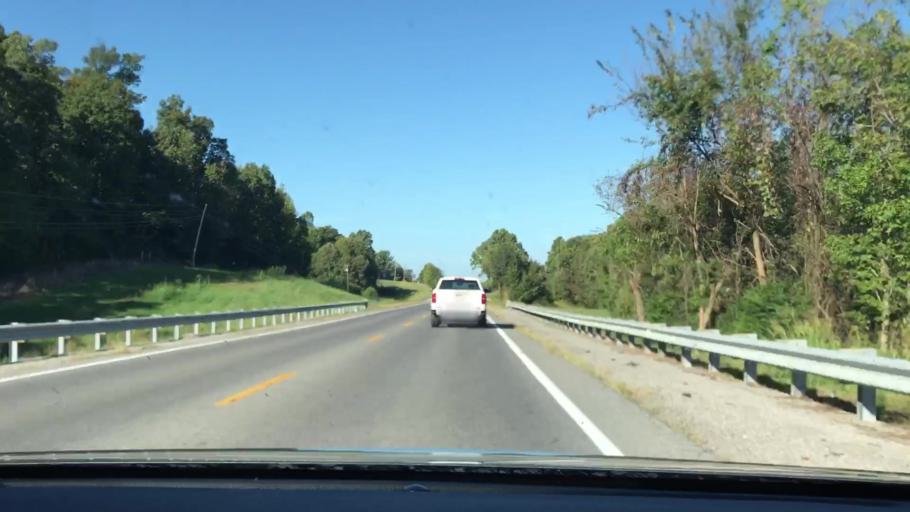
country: US
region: Kentucky
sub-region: Marshall County
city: Calvert City
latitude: 37.0047
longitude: -88.3793
